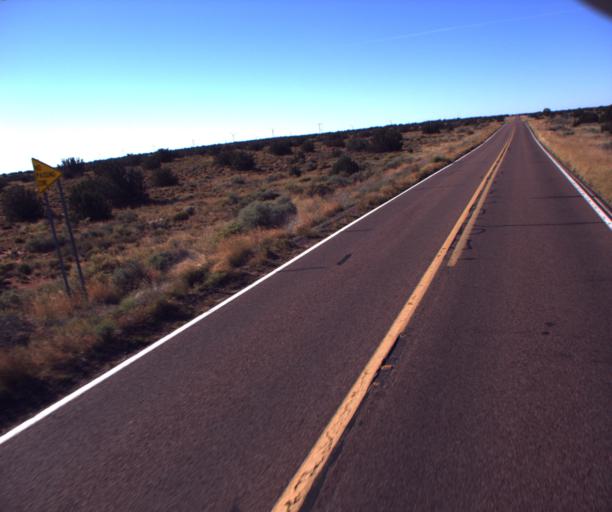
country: US
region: Arizona
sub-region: Navajo County
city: Holbrook
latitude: 34.7022
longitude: -110.3028
